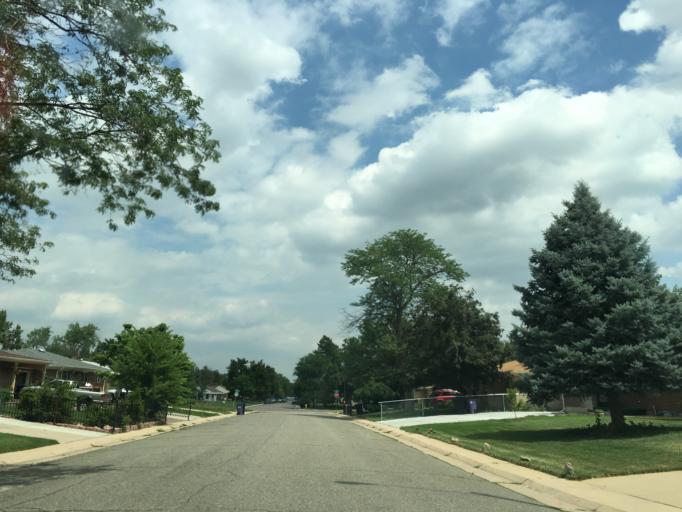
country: US
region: Colorado
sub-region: Arapahoe County
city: Sheridan
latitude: 39.6666
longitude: -105.0271
